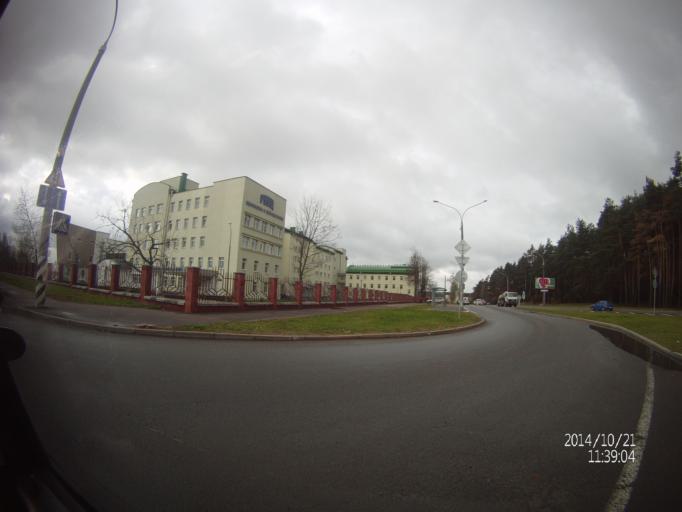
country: BY
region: Minsk
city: Borovlyany
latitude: 53.9242
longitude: 27.6788
